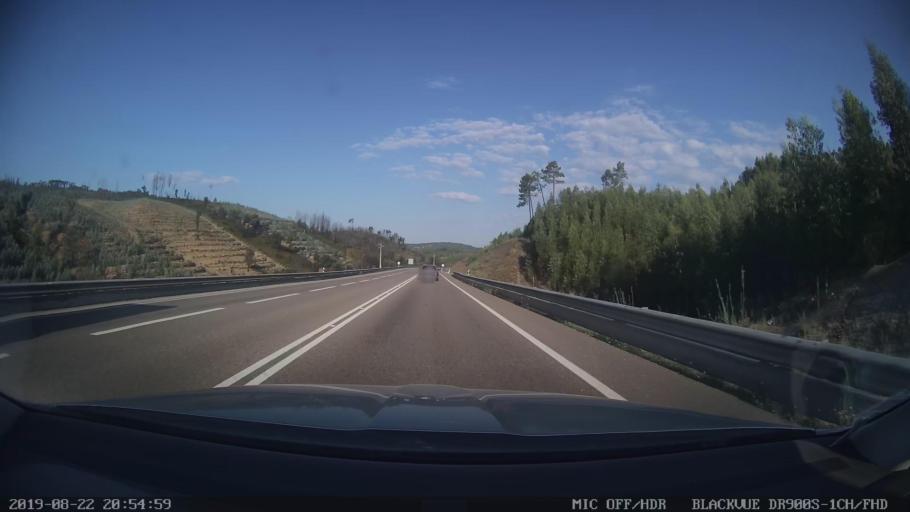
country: PT
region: Castelo Branco
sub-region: Serta
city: Serta
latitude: 39.7776
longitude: -8.0235
